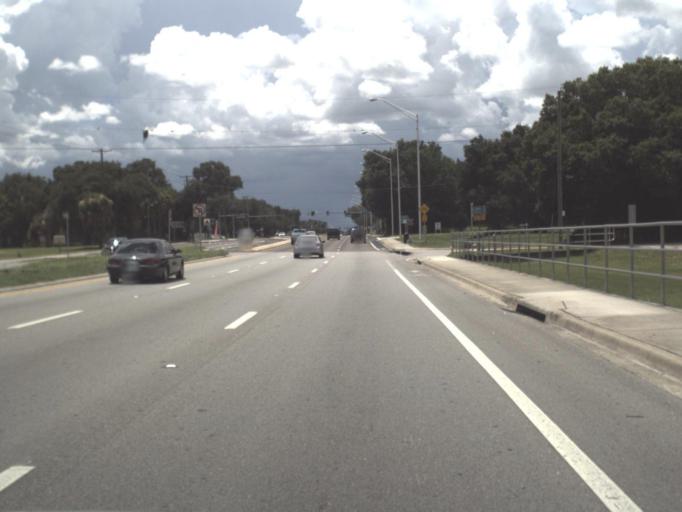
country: US
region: Florida
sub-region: Hillsborough County
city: Mango
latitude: 27.9817
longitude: -82.3036
